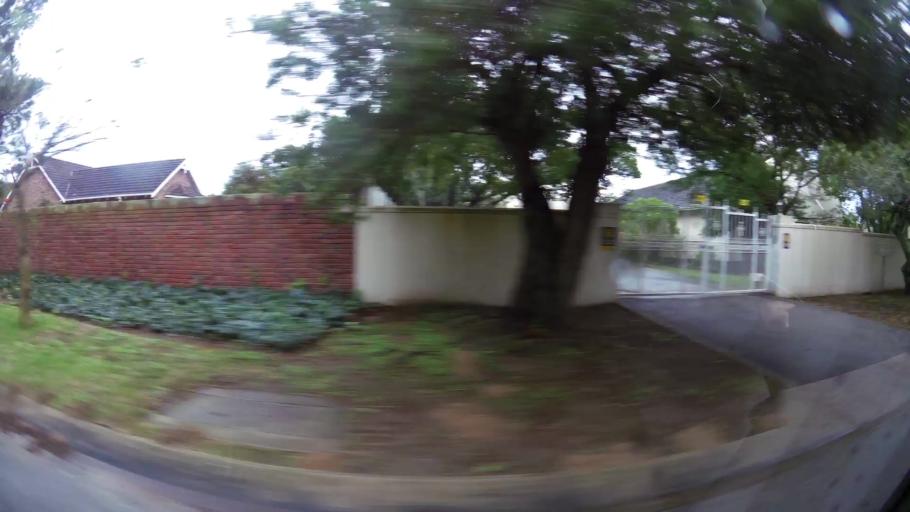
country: ZA
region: Eastern Cape
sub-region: Nelson Mandela Bay Metropolitan Municipality
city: Port Elizabeth
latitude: -33.9758
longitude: 25.5691
